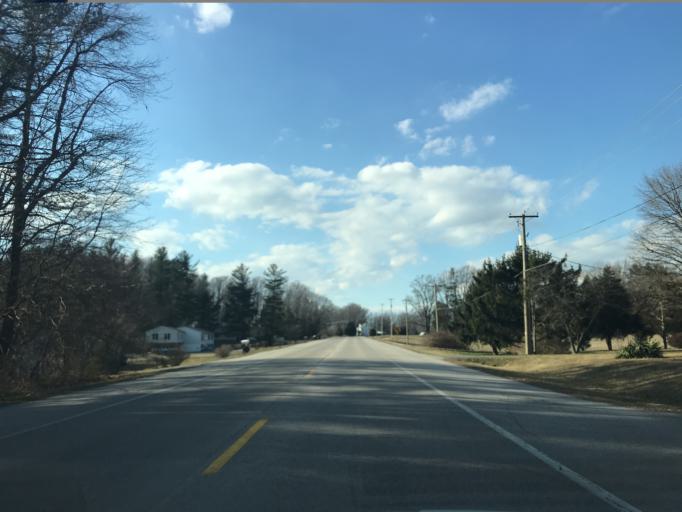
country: US
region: Maryland
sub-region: Cecil County
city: North East
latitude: 39.6512
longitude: -75.9730
